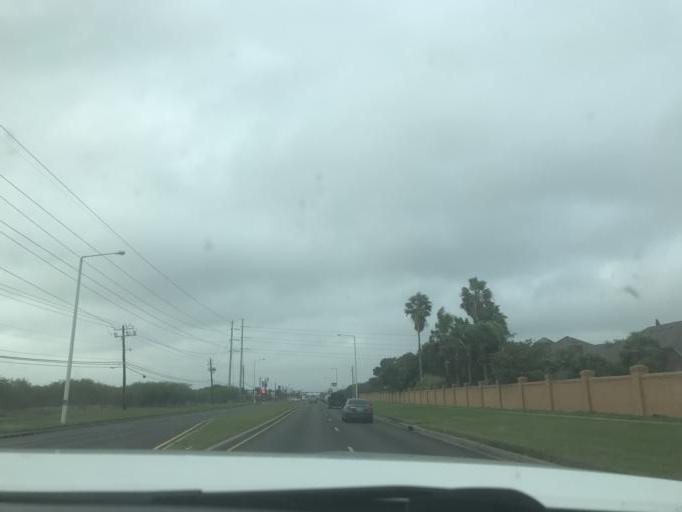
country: US
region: Texas
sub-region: Nueces County
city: Corpus Christi
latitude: 27.6811
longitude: -97.3749
